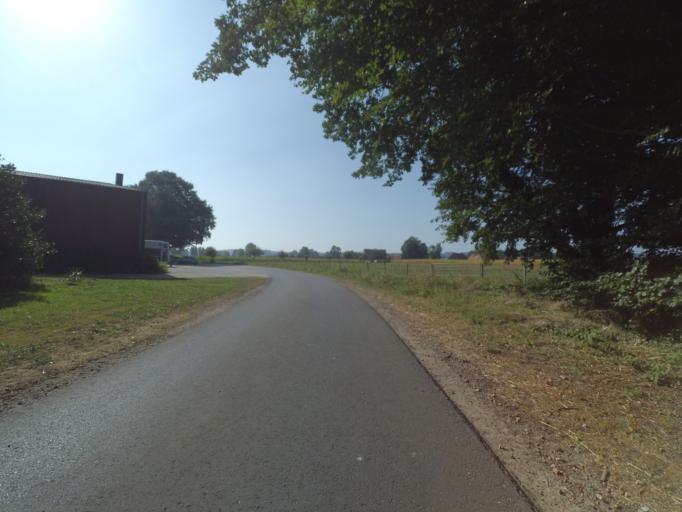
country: DE
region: North Rhine-Westphalia
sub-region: Regierungsbezirk Munster
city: Horstmar
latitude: 52.1165
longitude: 7.3049
